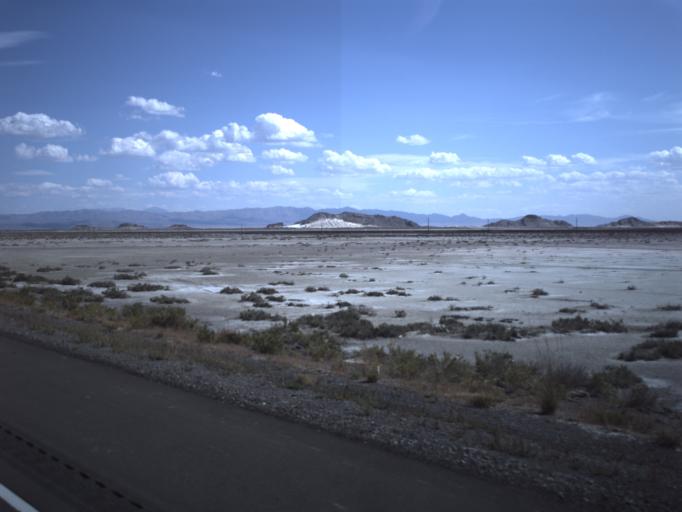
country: US
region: Utah
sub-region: Tooele County
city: Wendover
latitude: 40.7275
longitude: -113.3244
